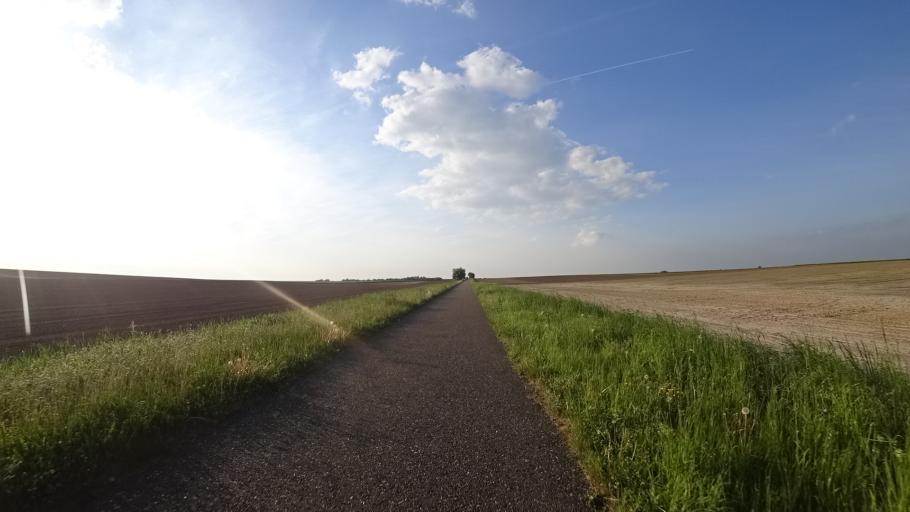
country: BE
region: Wallonia
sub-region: Province du Brabant Wallon
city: Ramillies
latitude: 50.6252
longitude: 4.8995
